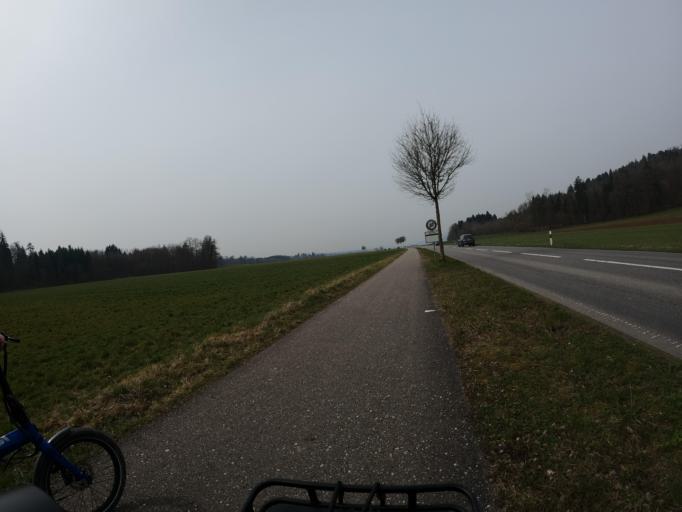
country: CH
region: Aargau
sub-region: Bezirk Lenzburg
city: Othmarsingen
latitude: 47.4160
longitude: 8.2128
